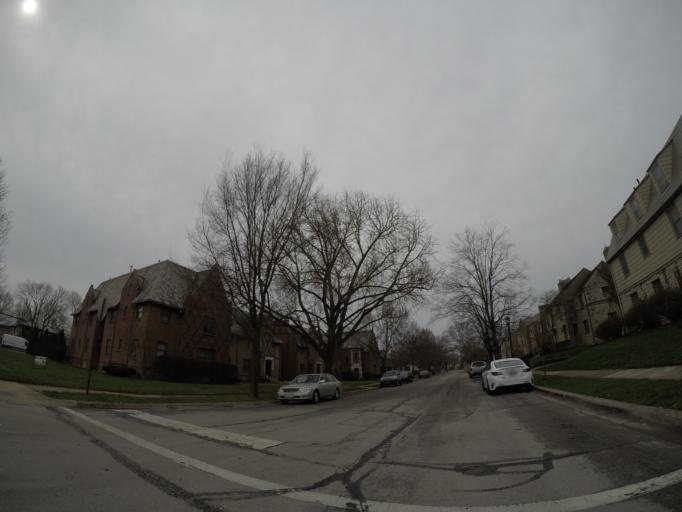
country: US
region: Ohio
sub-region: Franklin County
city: Upper Arlington
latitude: 40.0017
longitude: -83.0614
